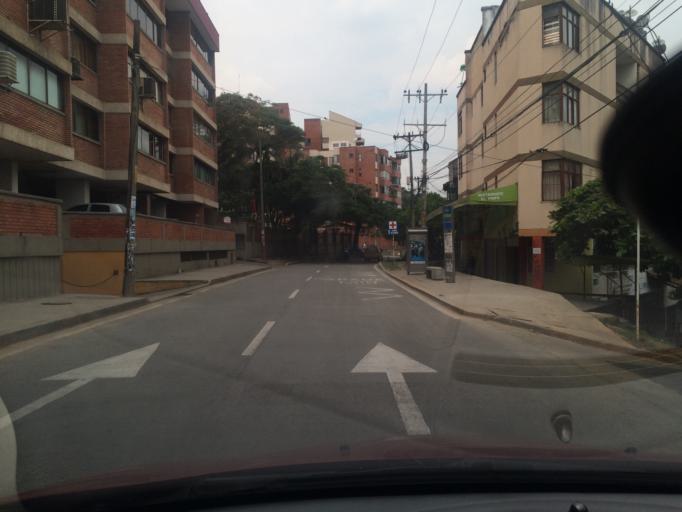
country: CO
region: Valle del Cauca
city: Cali
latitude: 3.4273
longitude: -76.5499
